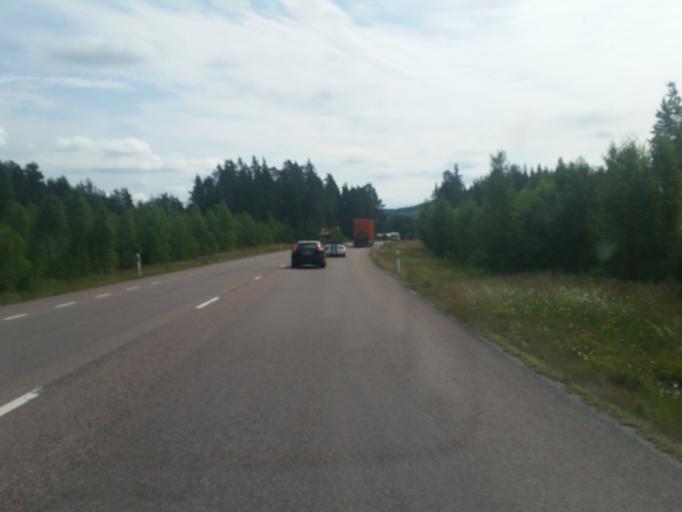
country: SE
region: Dalarna
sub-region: Gagnefs Kommun
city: Djuras
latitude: 60.5529
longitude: 15.2493
